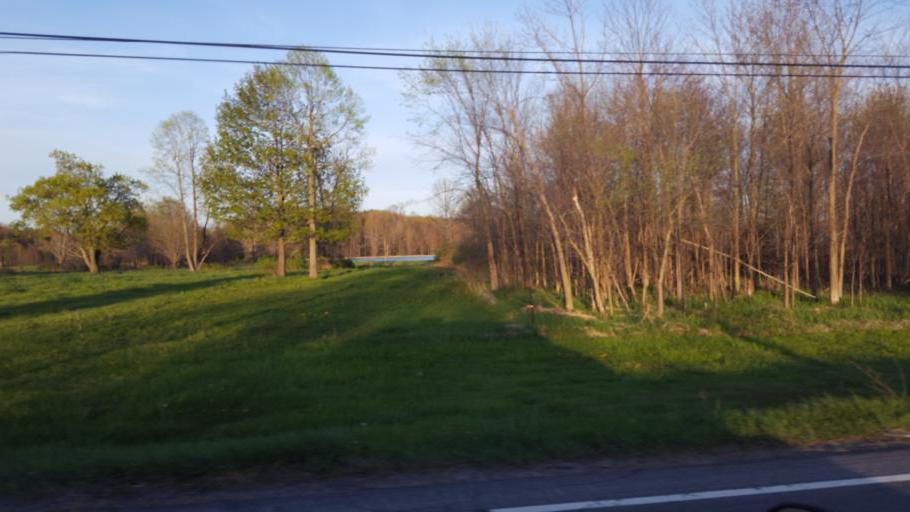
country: US
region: Ohio
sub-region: Ashtabula County
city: Andover
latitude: 41.5727
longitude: -80.5712
